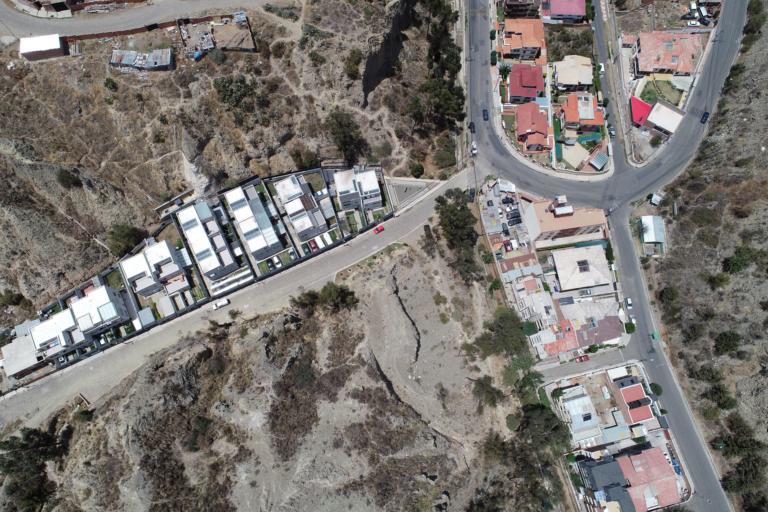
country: BO
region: La Paz
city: La Paz
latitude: -16.5223
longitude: -68.0789
